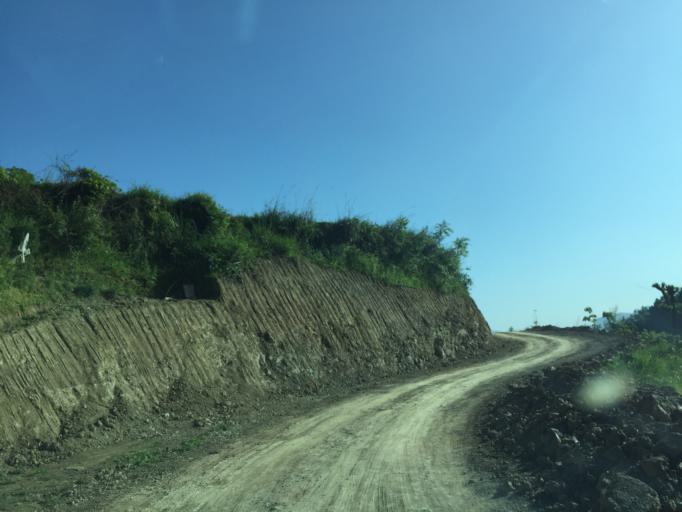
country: CN
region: Guizhou Sheng
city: Xujiaba
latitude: 27.7267
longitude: 108.0251
